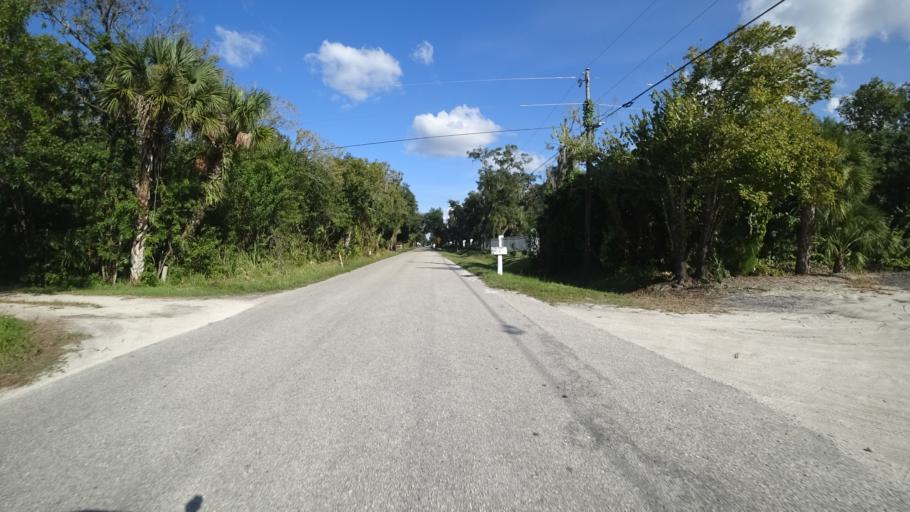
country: US
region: Florida
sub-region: Manatee County
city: Ellenton
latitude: 27.4829
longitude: -82.4845
